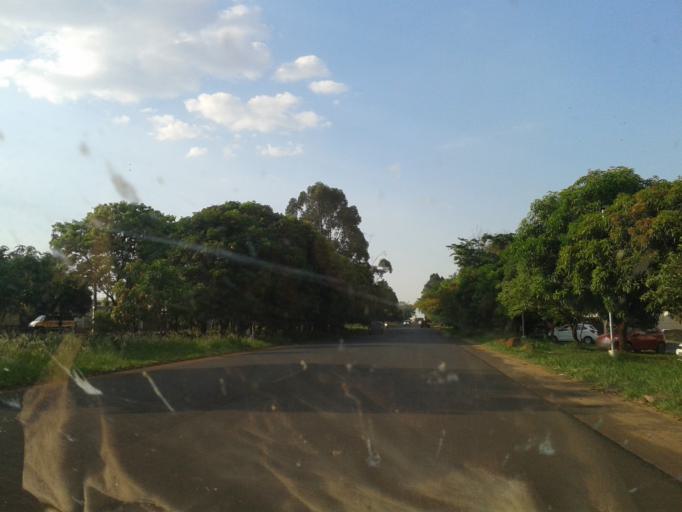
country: BR
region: Minas Gerais
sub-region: Uberlandia
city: Uberlandia
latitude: -18.9460
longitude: -48.3071
